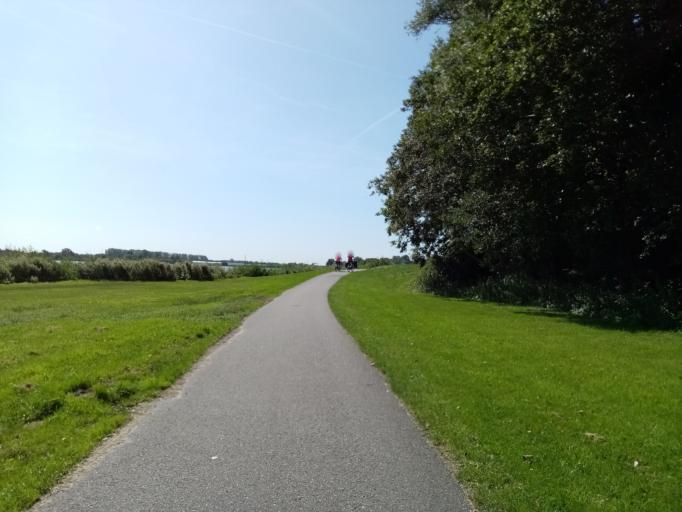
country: NL
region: South Holland
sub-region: Gemeente Noordwijkerhout
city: Noordwijkerhout
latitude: 52.2845
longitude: 4.5074
